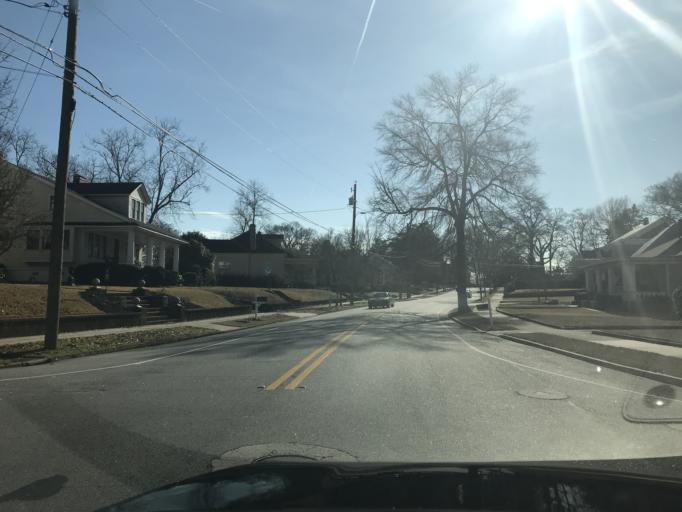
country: US
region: Georgia
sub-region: Coweta County
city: Newnan
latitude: 33.3701
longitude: -84.8011
